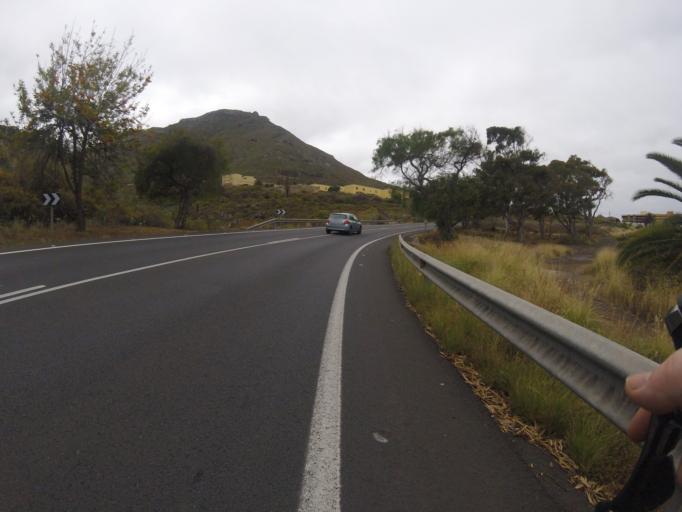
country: ES
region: Canary Islands
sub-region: Provincia de Santa Cruz de Tenerife
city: Tegueste
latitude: 28.5463
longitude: -16.3493
